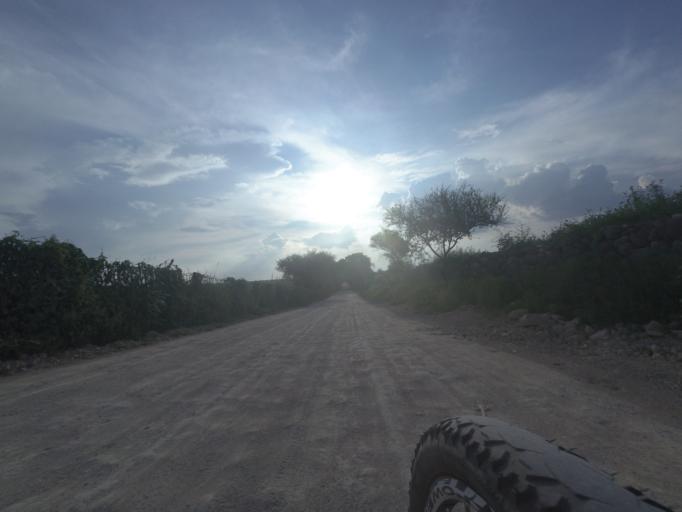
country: MX
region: Aguascalientes
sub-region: Aguascalientes
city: La Loma de los Negritos
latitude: 21.7753
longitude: -102.3645
